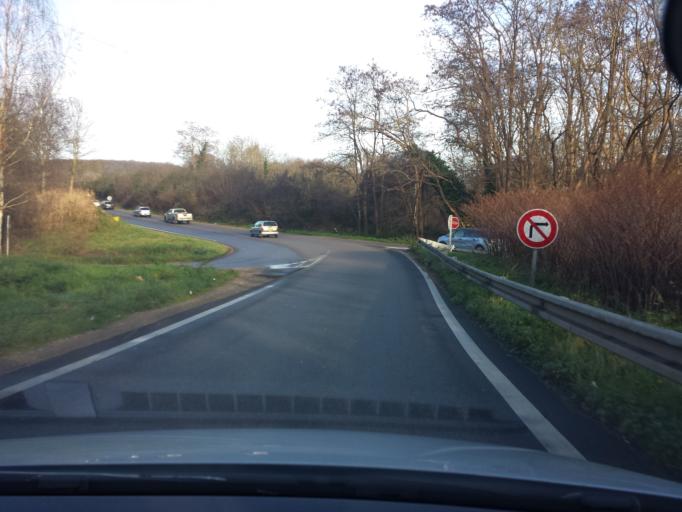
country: FR
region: Ile-de-France
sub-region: Departement de l'Essonne
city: Igny
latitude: 48.7467
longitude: 2.2198
